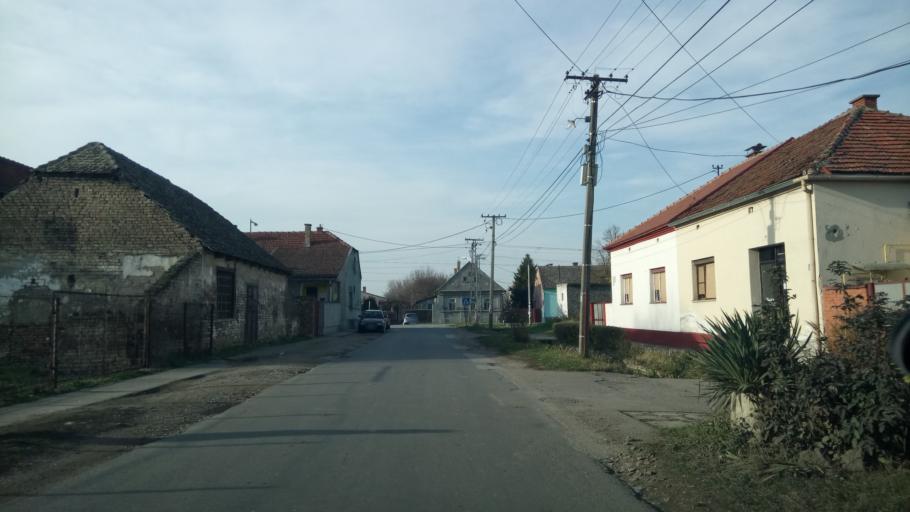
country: RS
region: Autonomna Pokrajina Vojvodina
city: Nova Pazova
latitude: 44.9454
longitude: 20.2216
